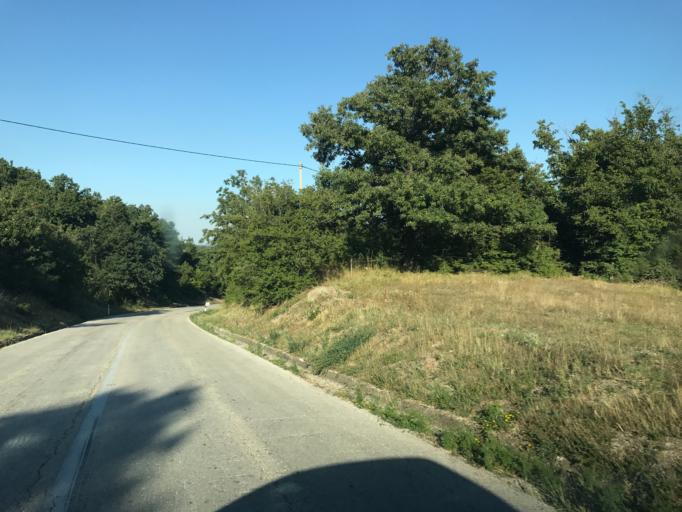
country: RO
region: Mehedinti
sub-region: Comuna Svinita
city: Svinita
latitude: 44.3002
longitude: 22.2553
